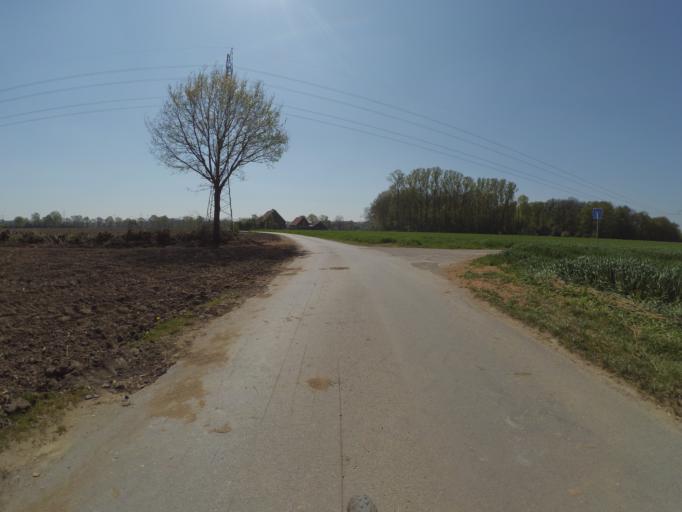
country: DE
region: North Rhine-Westphalia
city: Ludinghausen
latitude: 51.7492
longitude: 7.4408
